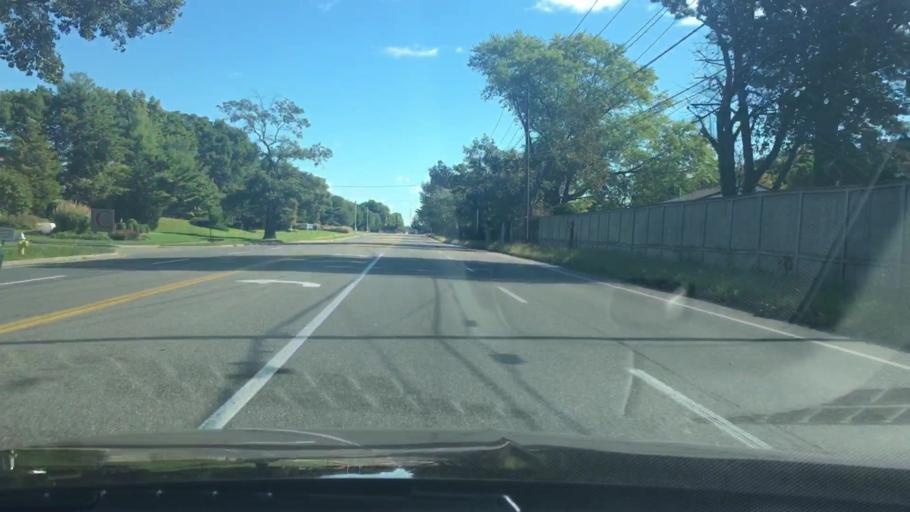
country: US
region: New York
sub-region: Suffolk County
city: Brentwood
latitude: 40.8062
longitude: -73.2615
